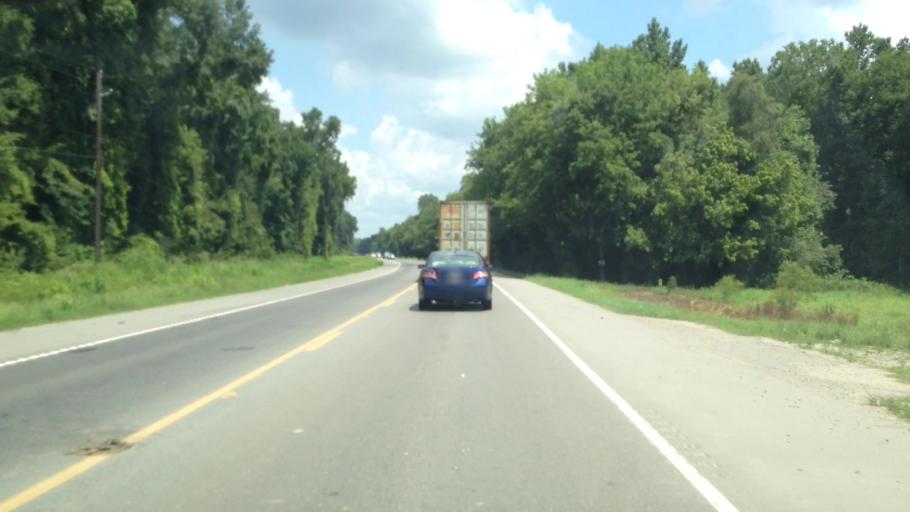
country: US
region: Louisiana
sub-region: Ascension Parish
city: Sorrento
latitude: 30.1527
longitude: -90.8749
